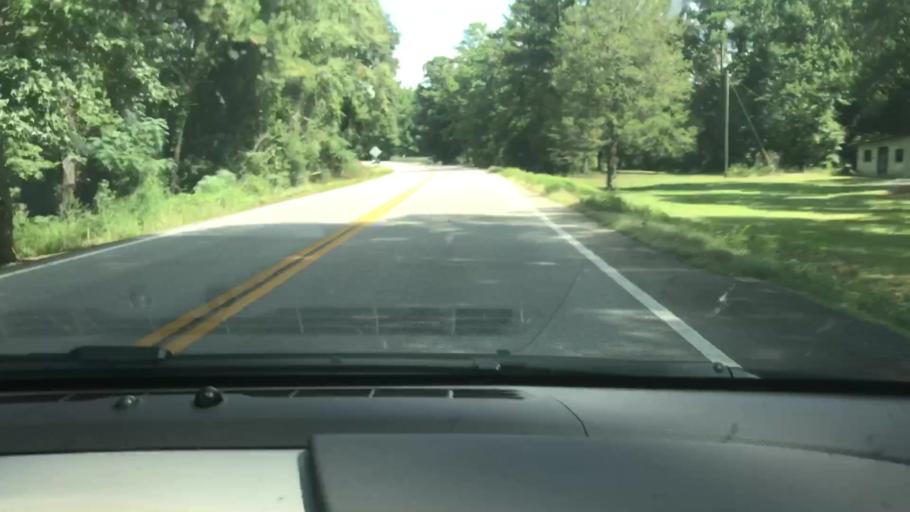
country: US
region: Georgia
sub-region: Troup County
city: La Grange
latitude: 32.9406
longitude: -85.0182
